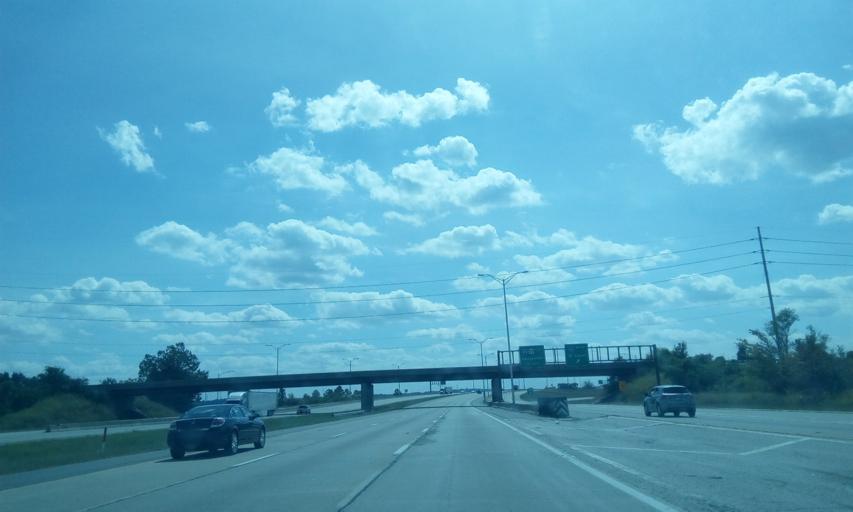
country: US
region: Illinois
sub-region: Saint Clair County
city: Washington Park
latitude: 38.6240
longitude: -90.0677
